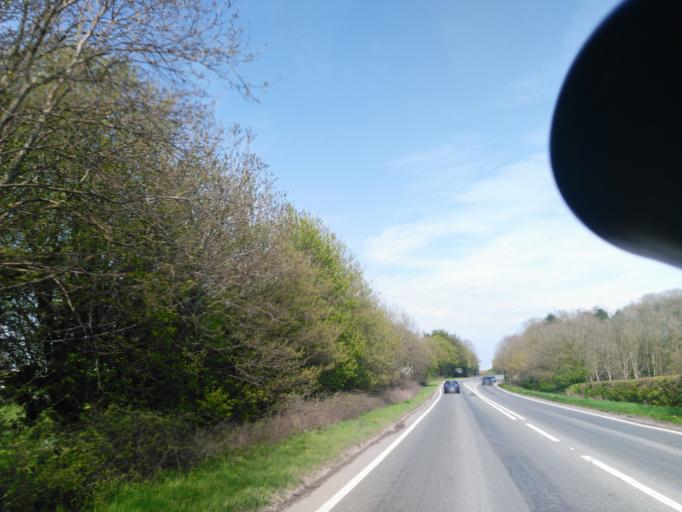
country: GB
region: England
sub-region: Somerset
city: Frome
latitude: 51.2042
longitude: -2.3618
